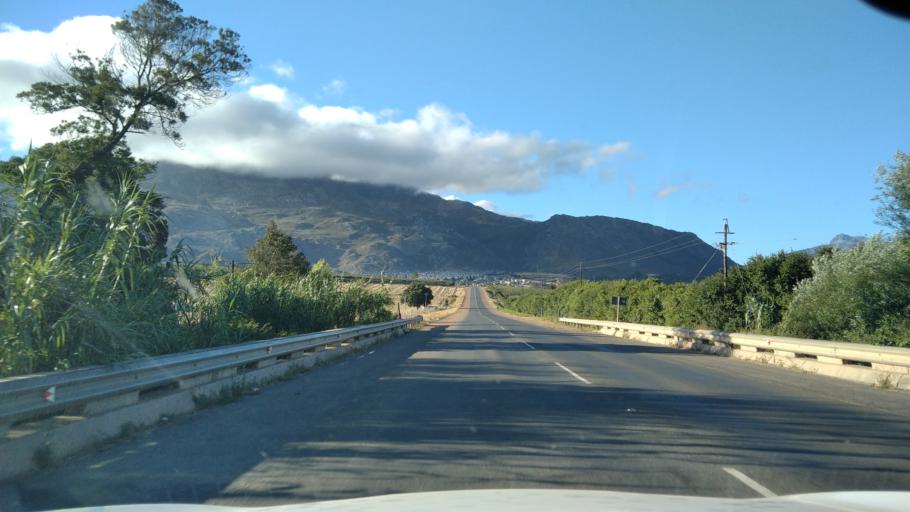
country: ZA
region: Western Cape
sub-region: Overberg District Municipality
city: Caledon
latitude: -34.0063
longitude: 19.2917
